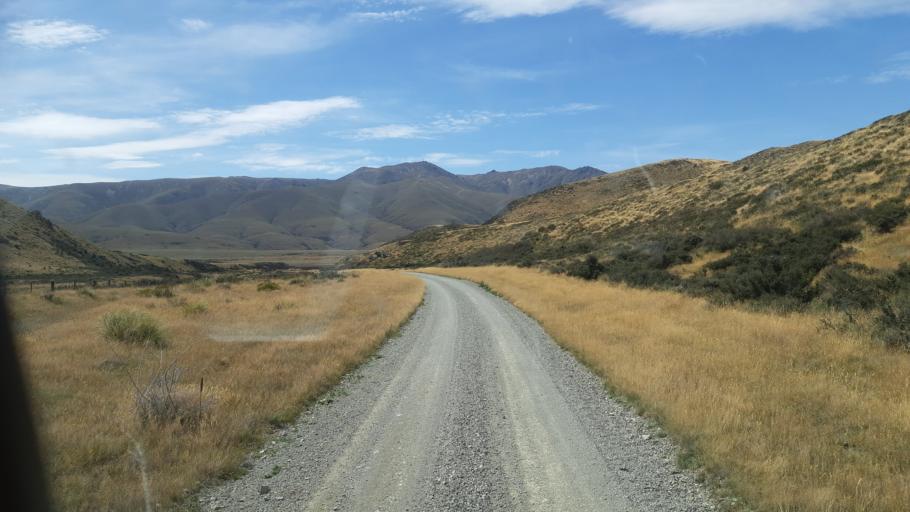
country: NZ
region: Canterbury
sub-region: Timaru District
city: Pleasant Point
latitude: -44.3534
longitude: 170.6129
